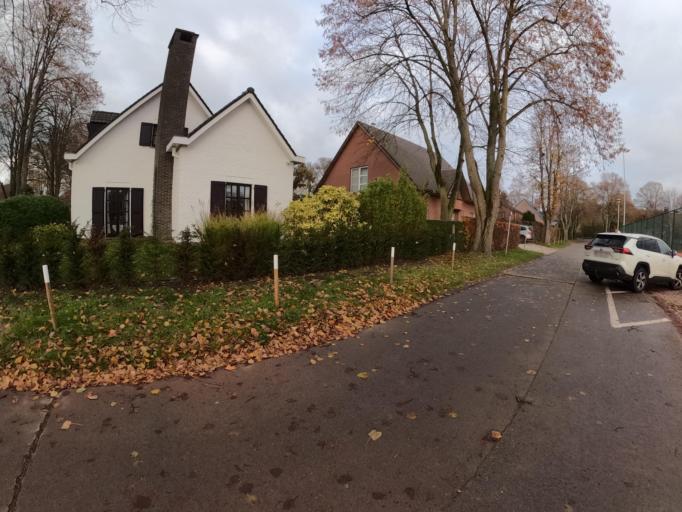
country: BE
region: Flanders
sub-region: Provincie Oost-Vlaanderen
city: Sint-Martens-Latem
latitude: 51.0141
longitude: 3.6324
